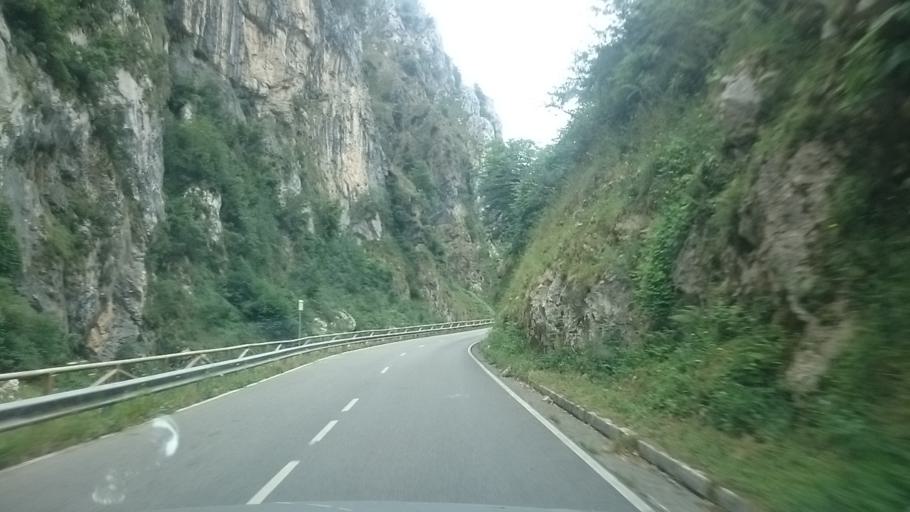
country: ES
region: Asturias
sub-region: Province of Asturias
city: Carrena
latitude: 43.2647
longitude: -4.8318
